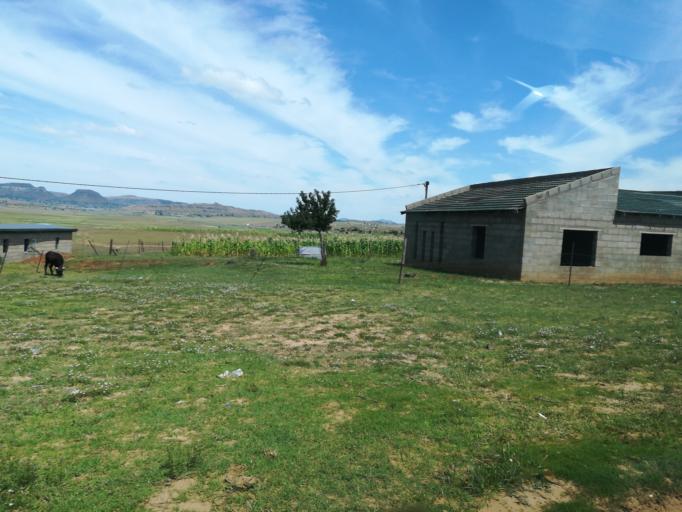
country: LS
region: Mohale's Hoek District
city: Mohale's Hoek
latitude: -30.1040
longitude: 27.4628
